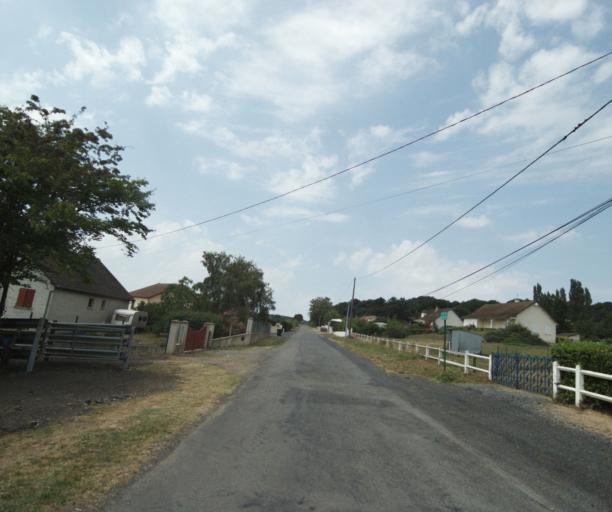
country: FR
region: Bourgogne
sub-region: Departement de Saone-et-Loire
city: Gueugnon
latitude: 46.5982
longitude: 4.0184
